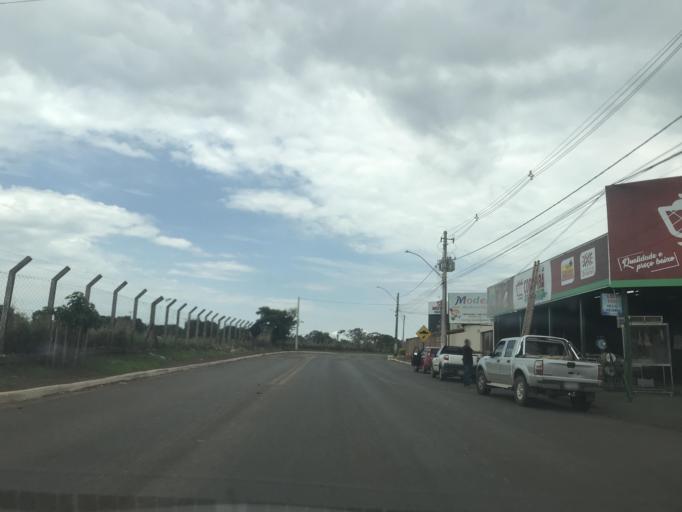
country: BR
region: Goias
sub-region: Luziania
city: Luziania
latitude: -16.2571
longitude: -47.9658
